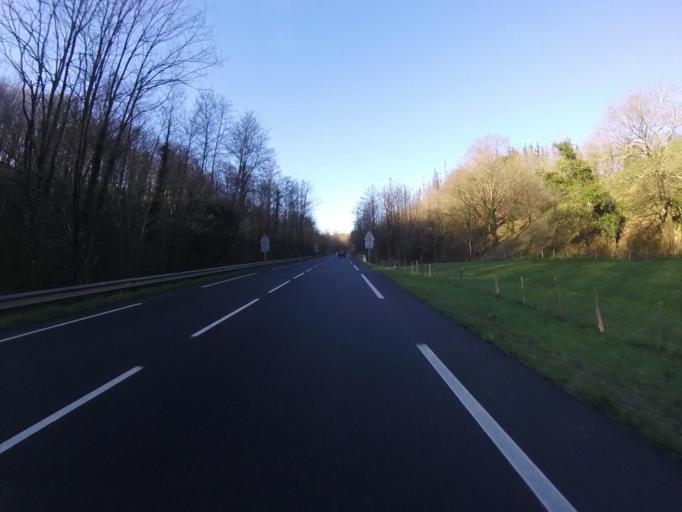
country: ES
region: Basque Country
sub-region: Provincia de Guipuzcoa
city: Errenteria
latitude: 43.2850
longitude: -1.9012
